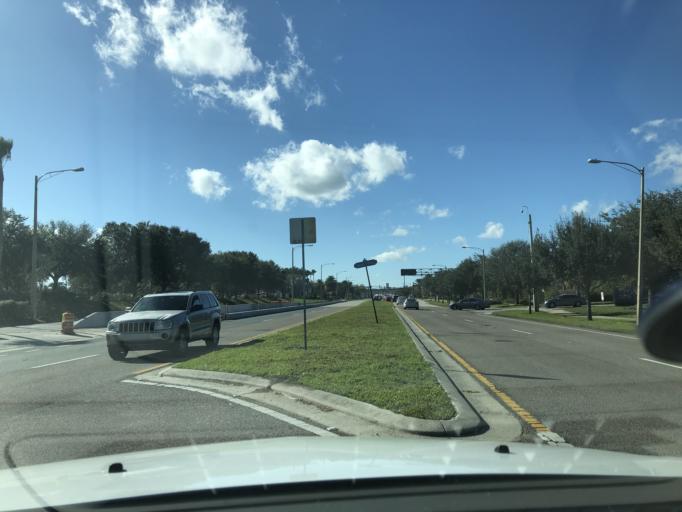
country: US
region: Florida
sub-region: Orange County
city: Tangelo Park
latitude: 28.4721
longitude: -81.4473
